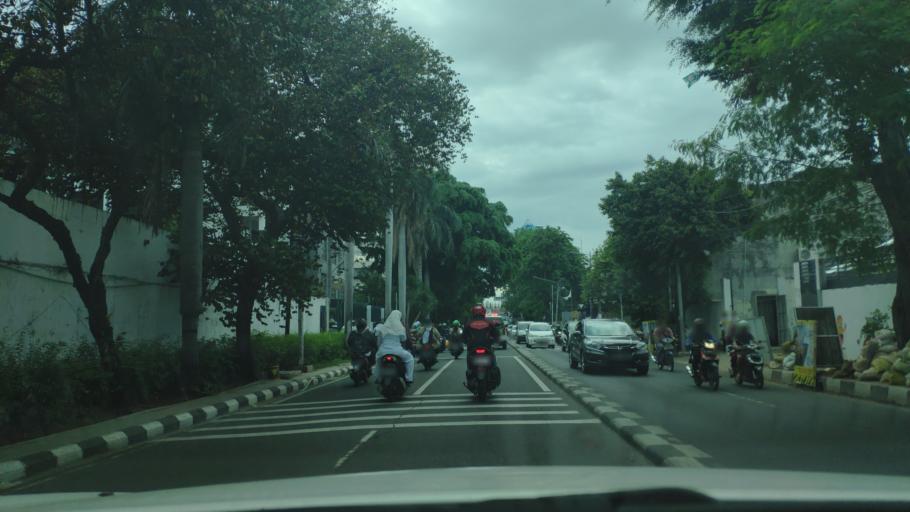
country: ID
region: Jakarta Raya
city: Jakarta
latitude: -6.1892
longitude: 106.8037
